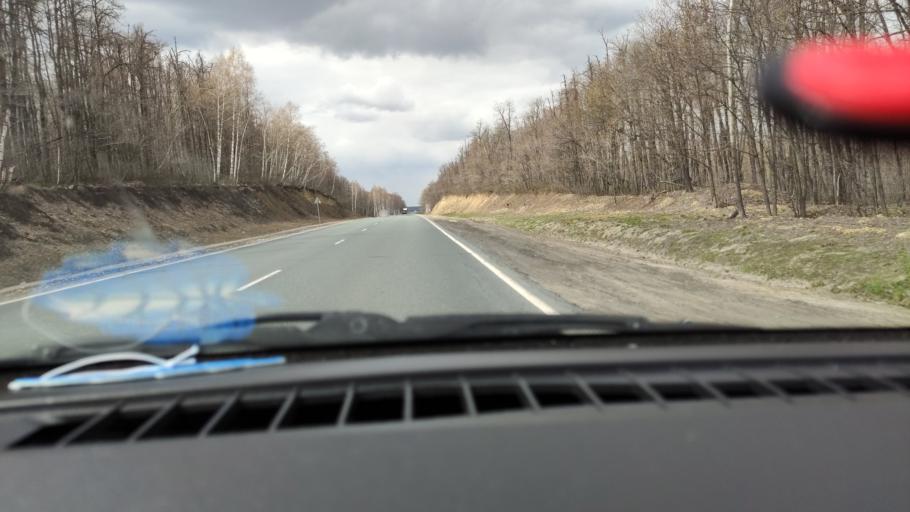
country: RU
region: Saratov
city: Vol'sk
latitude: 52.1116
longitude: 47.3330
